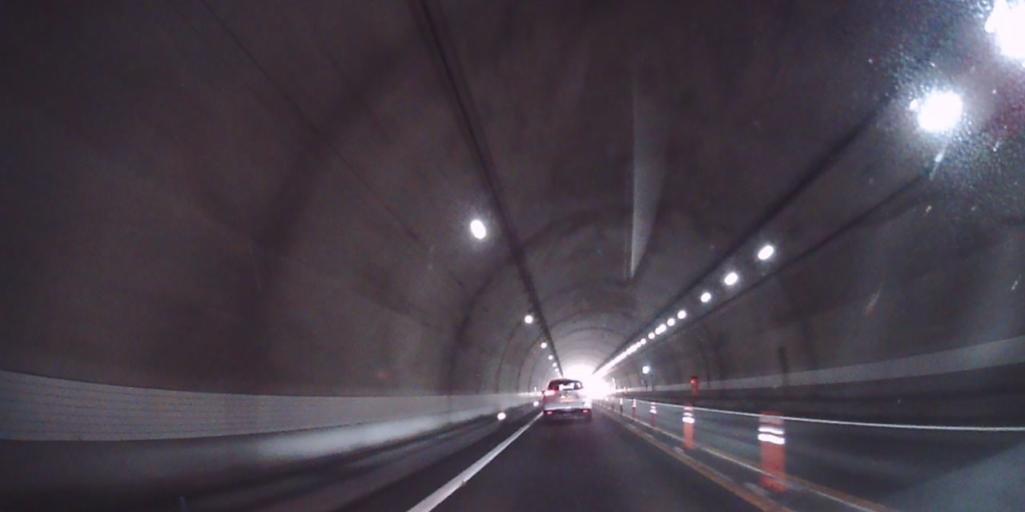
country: JP
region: Hokkaido
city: Niseko Town
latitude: 42.5946
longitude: 140.6726
